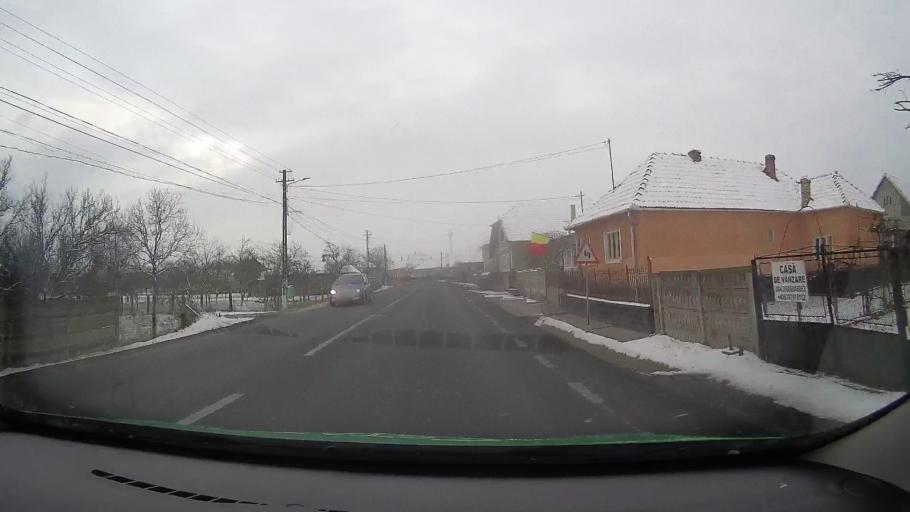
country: RO
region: Hunedoara
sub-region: Comuna Totesti
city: Totesti
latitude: 45.5761
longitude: 22.8878
